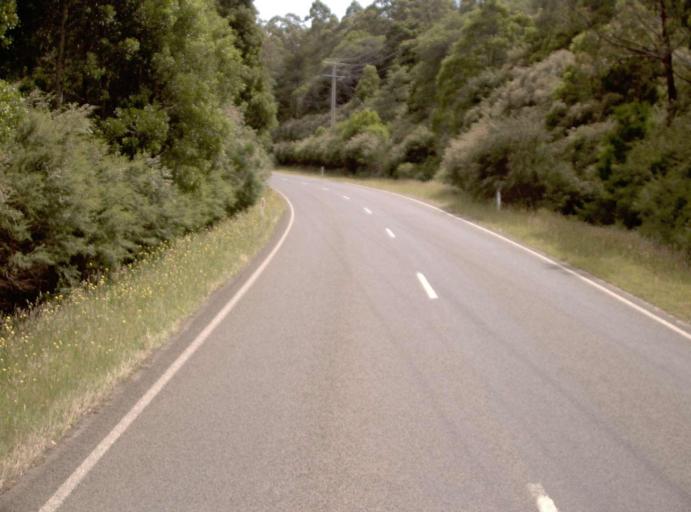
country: AU
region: Victoria
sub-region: Latrobe
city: Moe
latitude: -37.9387
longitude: 146.4027
